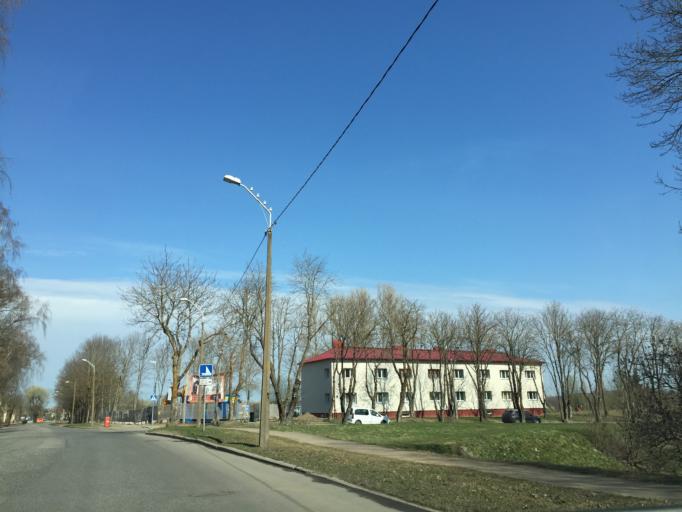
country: EE
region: Ida-Virumaa
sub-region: Narva linn
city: Narva
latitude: 59.3835
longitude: 28.2003
